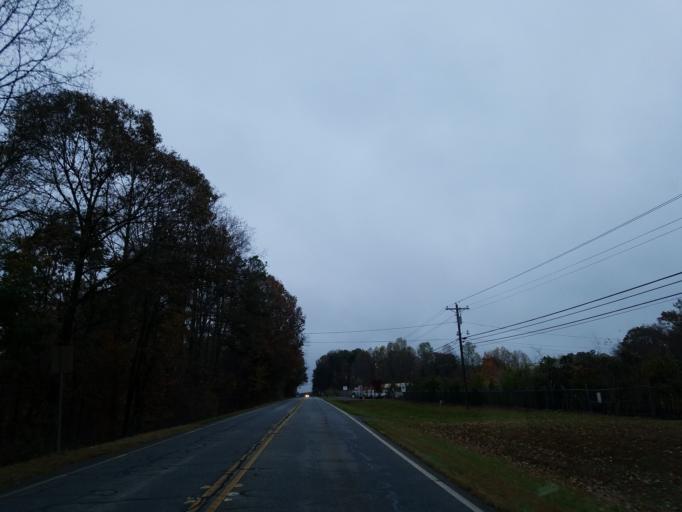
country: US
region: Georgia
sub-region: Pickens County
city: Jasper
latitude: 34.3793
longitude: -84.4765
